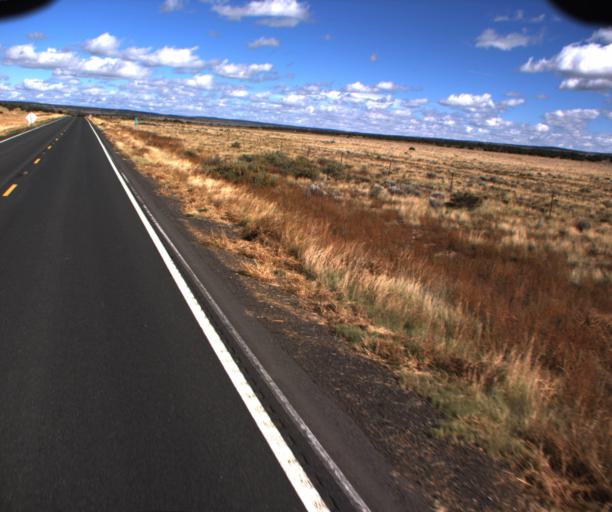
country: US
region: Arizona
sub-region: Apache County
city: Houck
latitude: 34.9928
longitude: -109.2272
